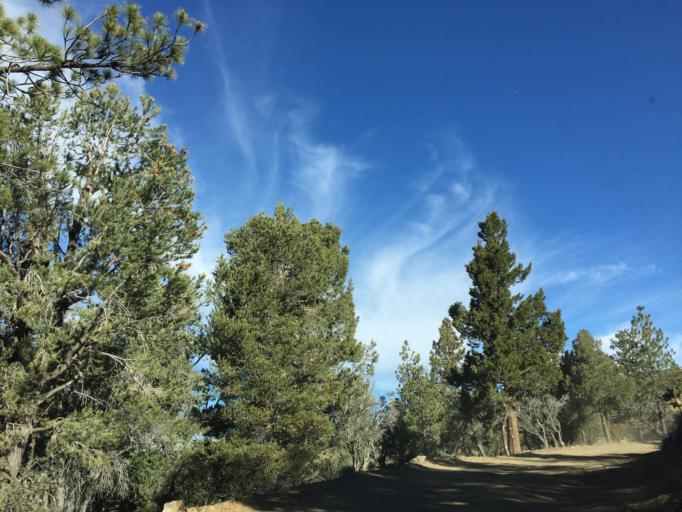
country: US
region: California
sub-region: San Bernardino County
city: Big Bear City
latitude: 34.2091
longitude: -116.7304
